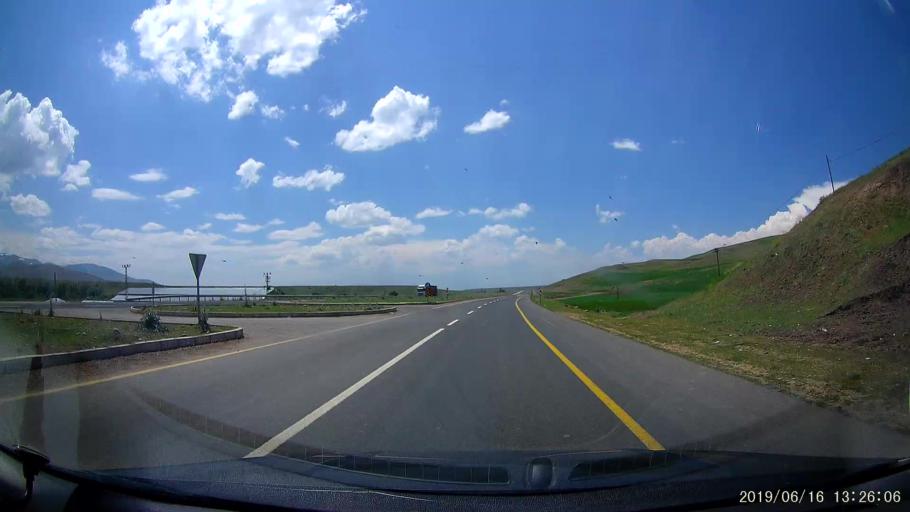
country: TR
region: Agri
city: Taslicay
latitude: 39.6572
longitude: 43.3361
